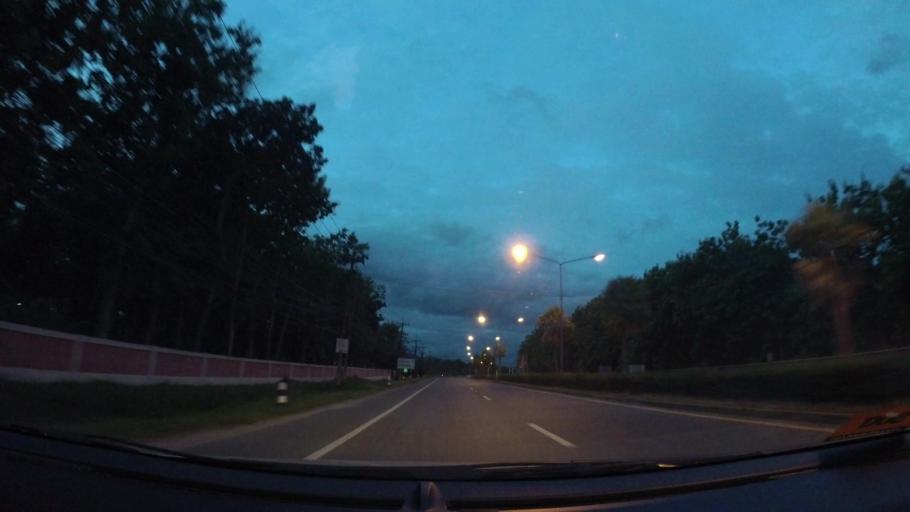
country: TH
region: Rayong
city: Ban Chang
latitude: 12.6918
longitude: 100.9821
